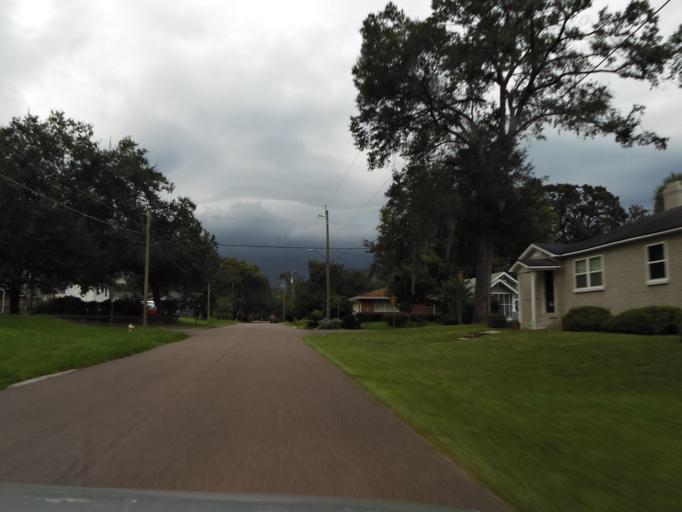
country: US
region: Florida
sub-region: Duval County
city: Jacksonville
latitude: 30.2959
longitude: -81.7115
